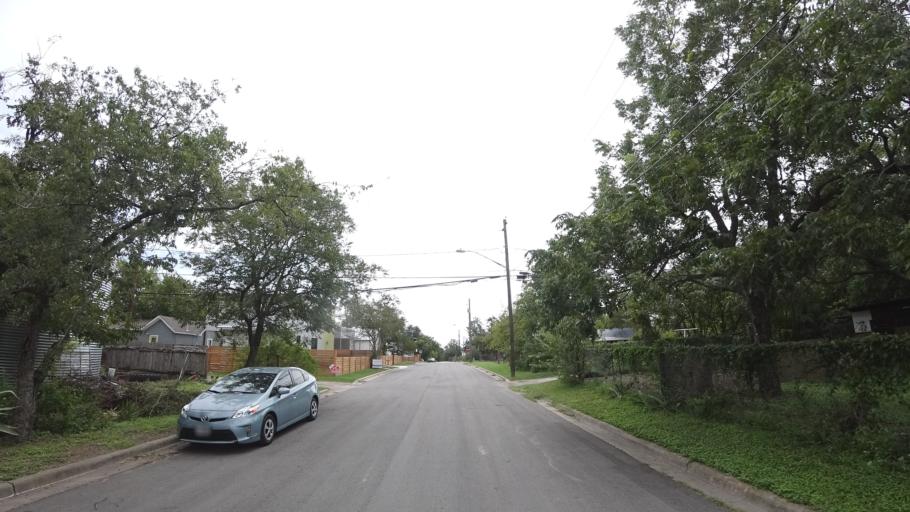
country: US
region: Texas
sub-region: Travis County
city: Austin
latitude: 30.2768
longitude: -97.7185
